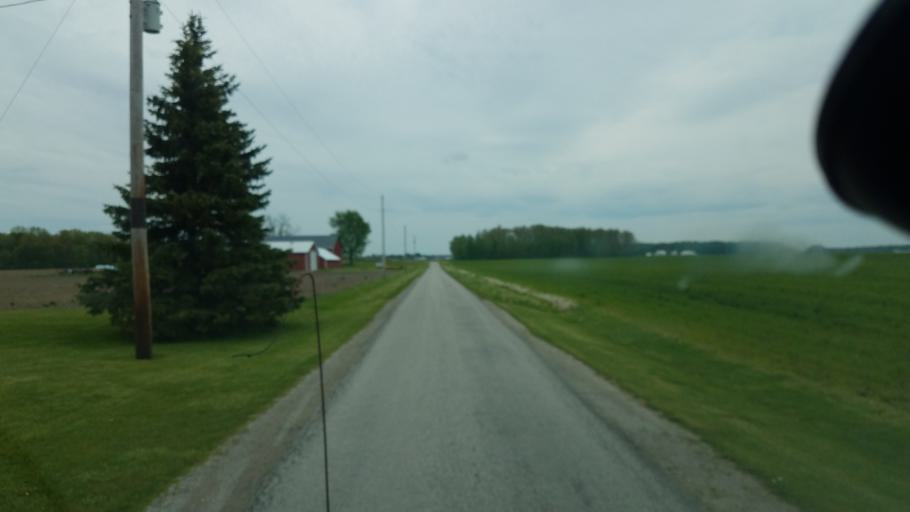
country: US
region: Ohio
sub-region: Huron County
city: Willard
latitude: 41.0101
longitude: -82.7979
